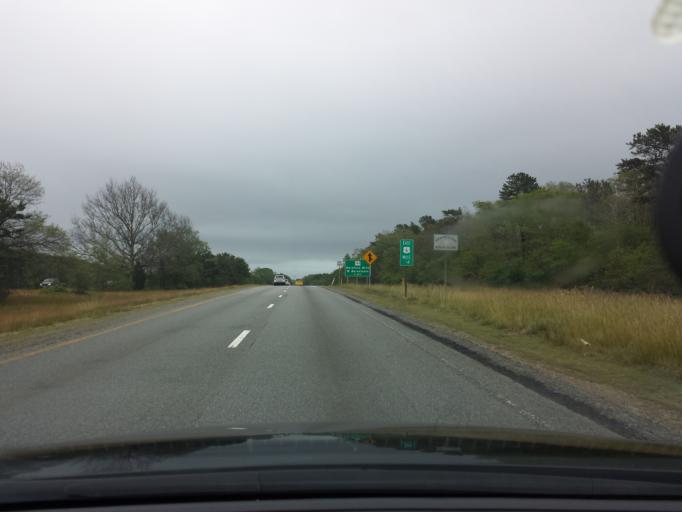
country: US
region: Massachusetts
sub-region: Barnstable County
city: West Barnstable
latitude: 41.7077
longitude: -70.4075
